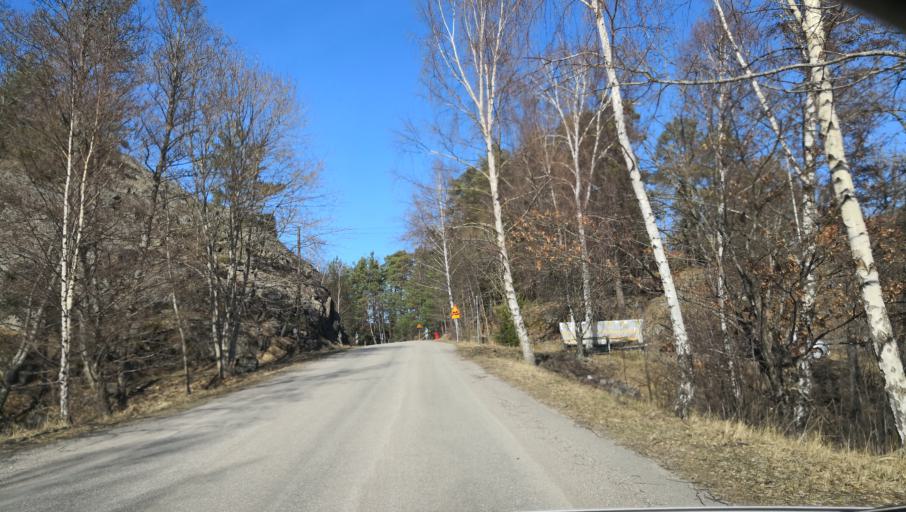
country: SE
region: Stockholm
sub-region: Varmdo Kommun
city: Mortnas
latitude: 59.2950
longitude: 18.4191
